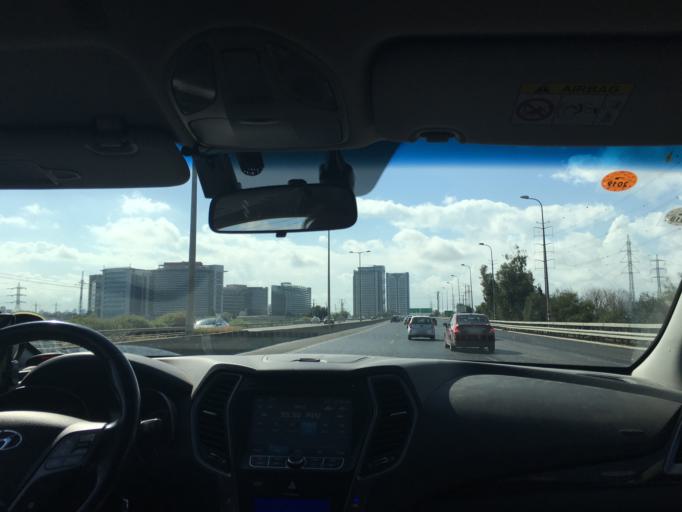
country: IL
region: Tel Aviv
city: Giv`at Shemu'el
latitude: 32.1068
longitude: 34.8490
